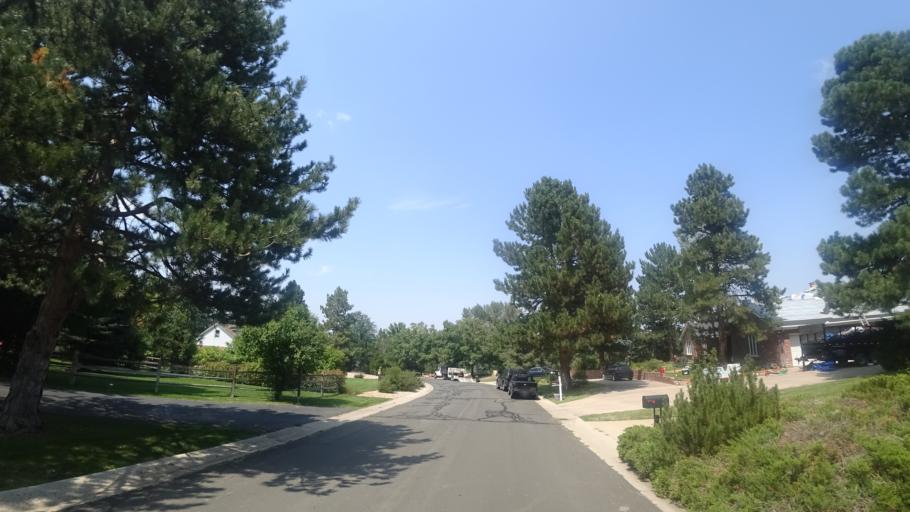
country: US
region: Colorado
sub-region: Arapahoe County
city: Greenwood Village
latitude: 39.6204
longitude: -104.9667
